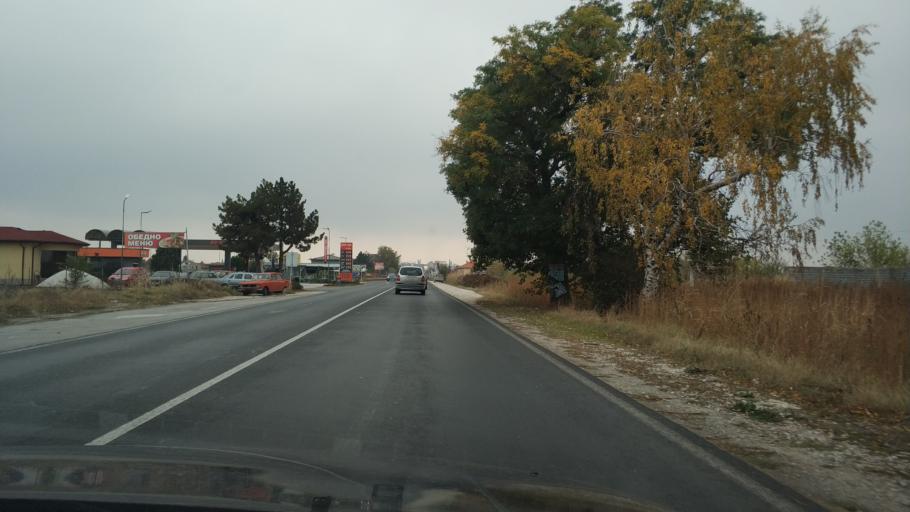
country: BG
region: Plovdiv
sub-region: Obshtina Plovdiv
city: Plovdiv
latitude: 42.2411
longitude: 24.7235
